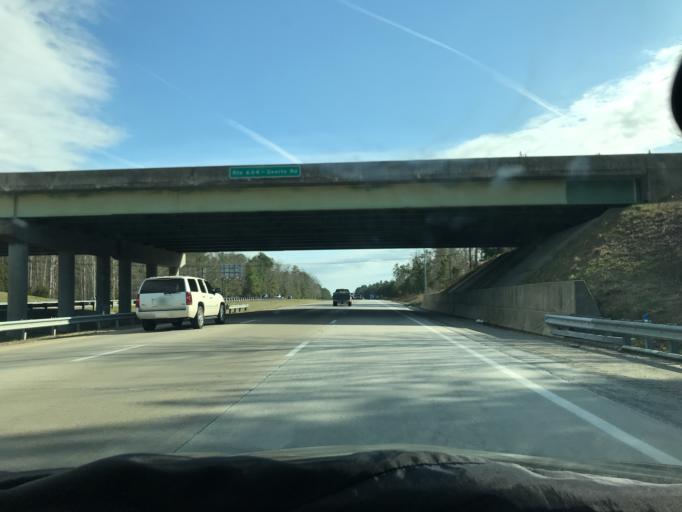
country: US
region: Virginia
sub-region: Chesterfield County
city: Brandermill
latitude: 37.4509
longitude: -77.6374
